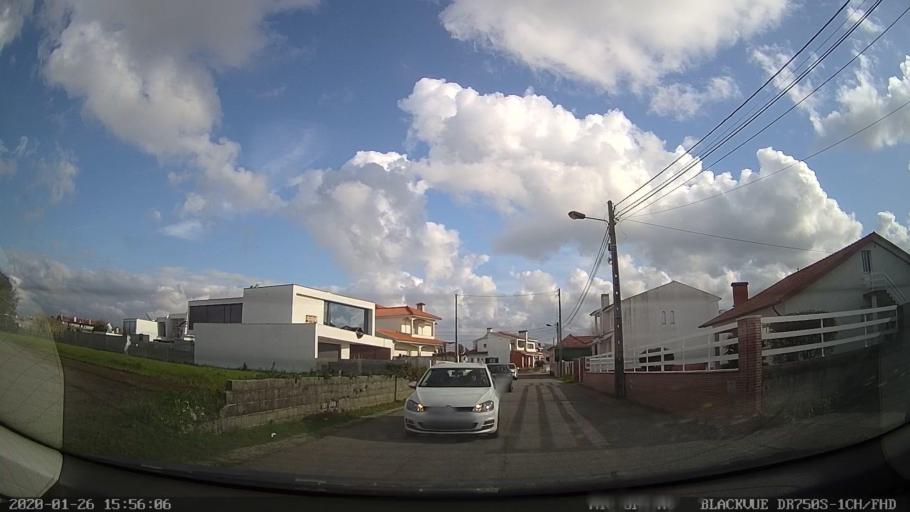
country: PT
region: Aveiro
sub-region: Aveiro
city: Aradas
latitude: 40.6307
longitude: -8.6299
